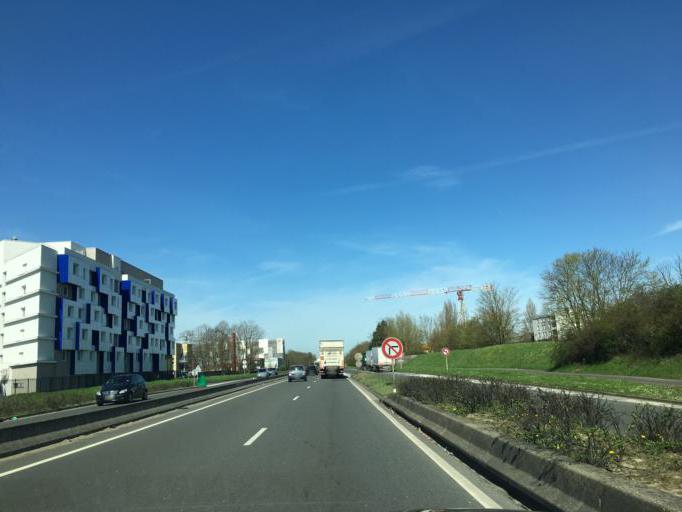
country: FR
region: Ile-de-France
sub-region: Departement de l'Essonne
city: Evry
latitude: 48.6231
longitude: 2.4480
